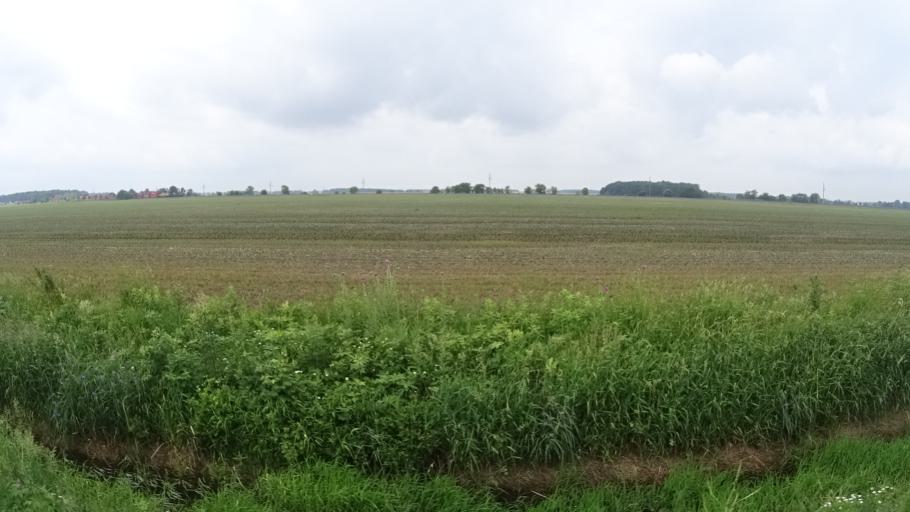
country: US
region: Ohio
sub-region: Huron County
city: Bellevue
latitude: 41.3104
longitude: -82.8050
